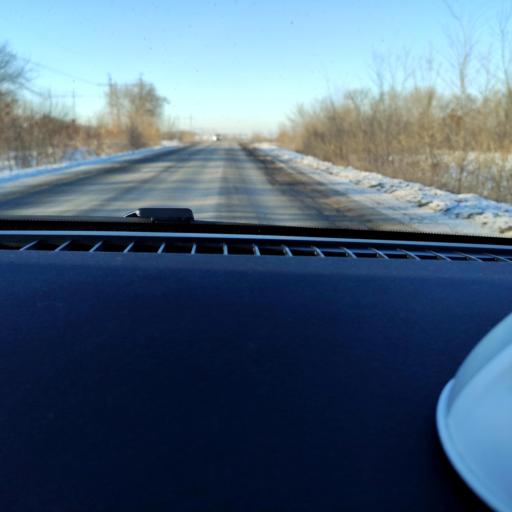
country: RU
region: Samara
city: Spiridonovka
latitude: 53.1445
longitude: 50.5270
